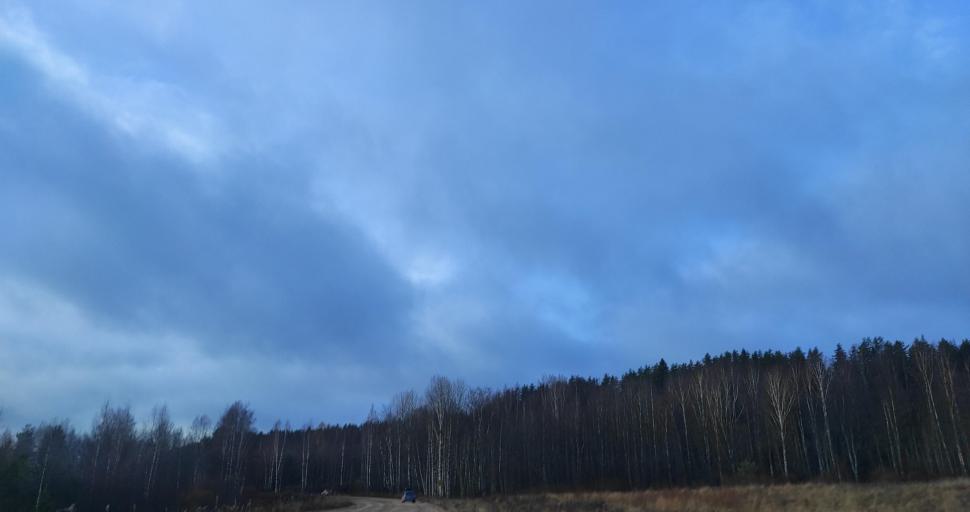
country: RU
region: Republic of Karelia
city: Pitkyaranta
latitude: 61.7129
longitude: 31.3347
